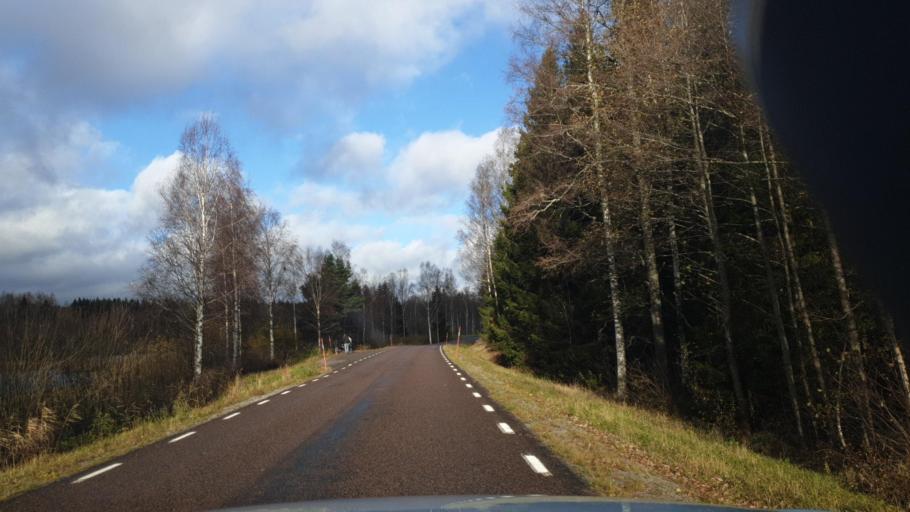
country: SE
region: Vaermland
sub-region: Grums Kommun
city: Slottsbron
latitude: 59.4797
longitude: 12.8845
